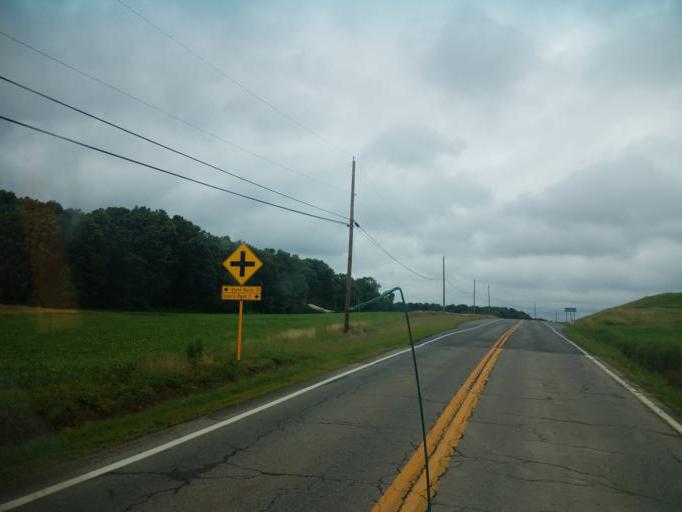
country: US
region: Ohio
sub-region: Carroll County
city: Carrollton
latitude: 40.6172
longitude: -81.0678
